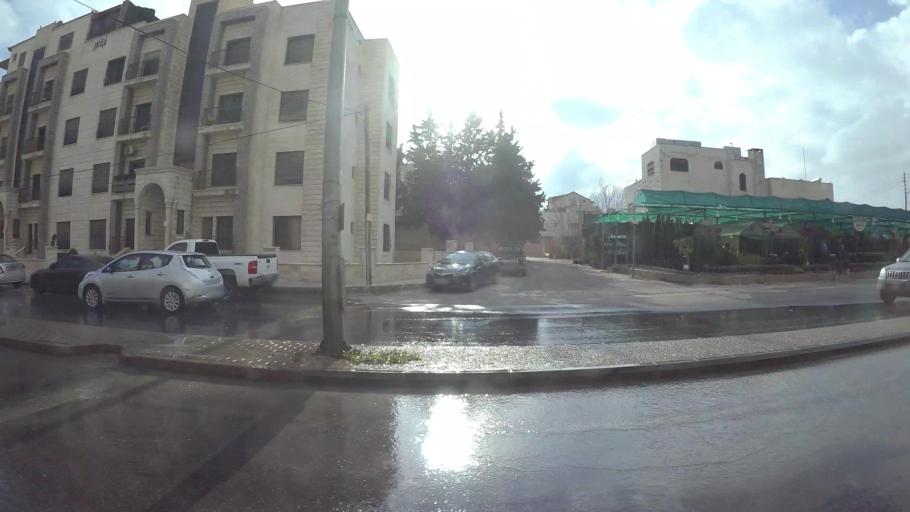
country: JO
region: Amman
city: Wadi as Sir
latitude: 31.9823
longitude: 35.8387
